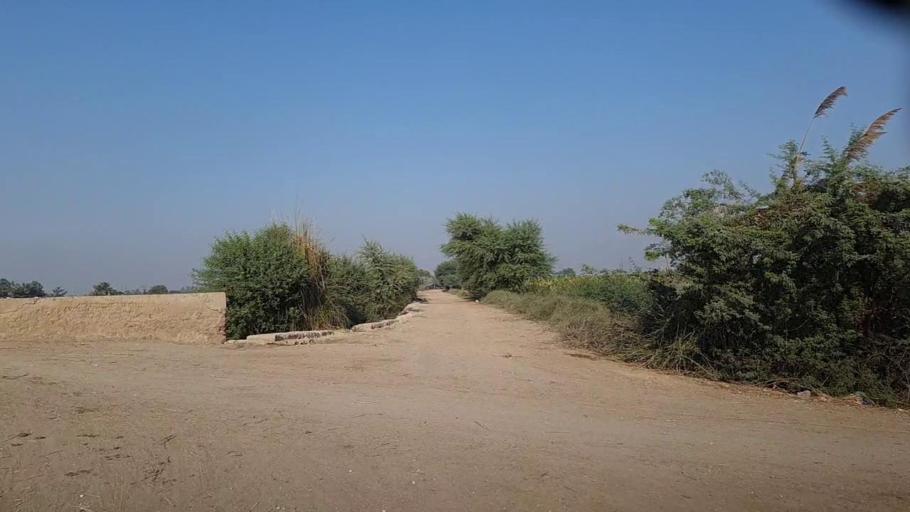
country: PK
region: Sindh
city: Ranipur
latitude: 27.2502
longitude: 68.5575
